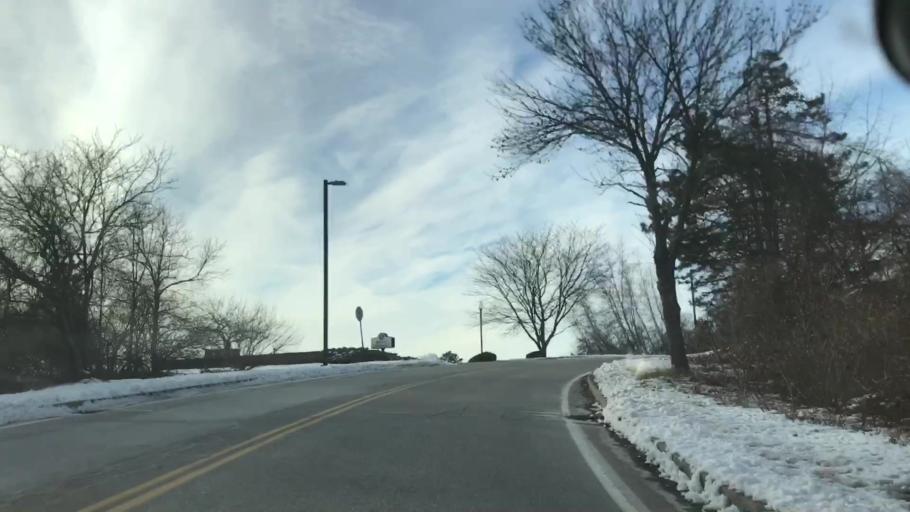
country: US
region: New Hampshire
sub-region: Merrimack County
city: South Hooksett
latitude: 43.0468
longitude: -71.4637
